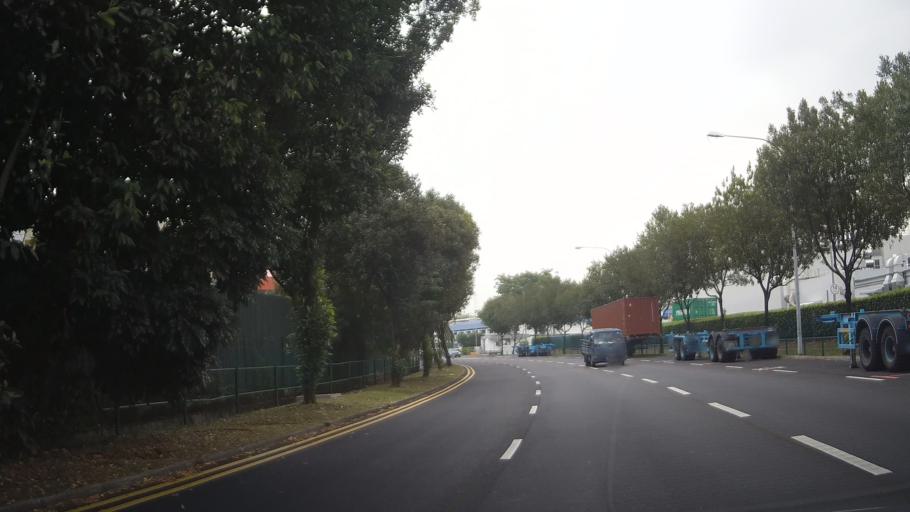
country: MY
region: Johor
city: Johor Bahru
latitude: 1.3194
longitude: 103.6644
